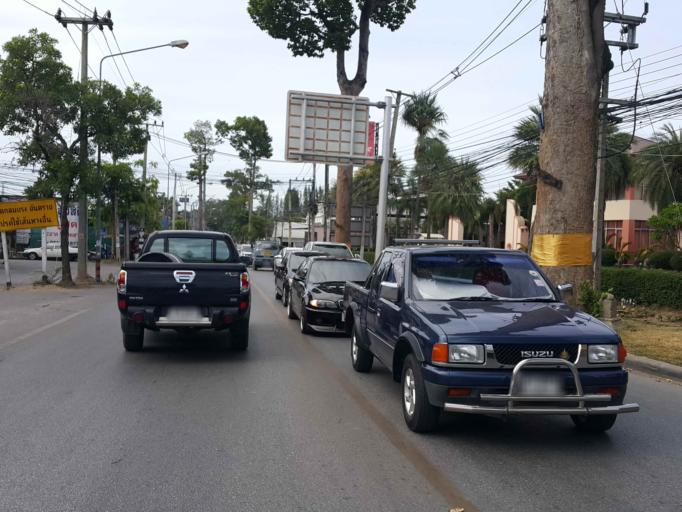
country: TH
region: Chiang Mai
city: Chiang Mai
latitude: 18.7576
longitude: 99.0075
